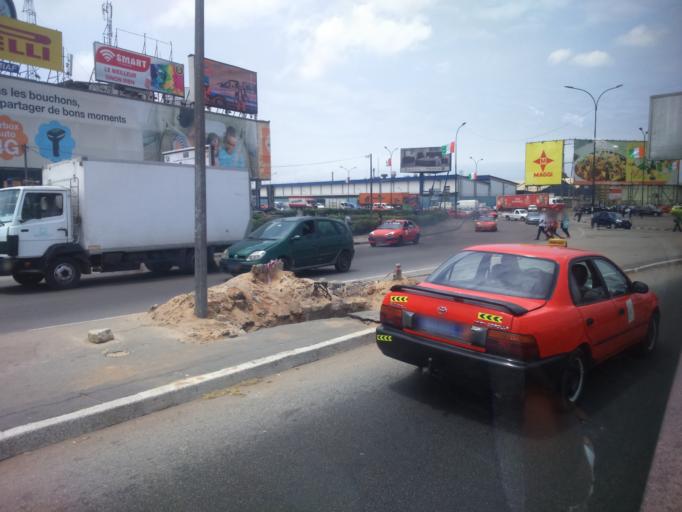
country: CI
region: Lagunes
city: Abidjan
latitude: 5.3021
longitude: -3.9941
